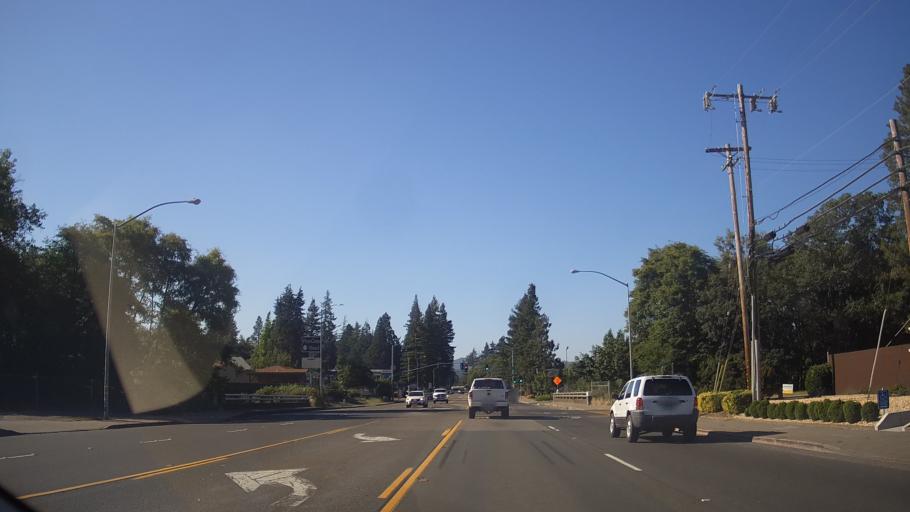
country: US
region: California
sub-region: Mendocino County
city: Willits
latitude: 39.3971
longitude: -123.3494
